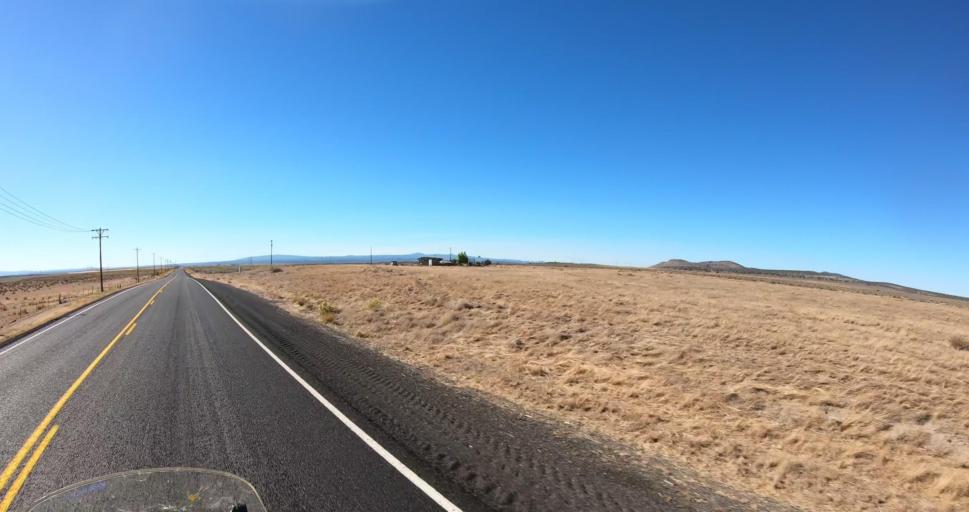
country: US
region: Oregon
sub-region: Deschutes County
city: La Pine
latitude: 43.1302
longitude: -120.9214
